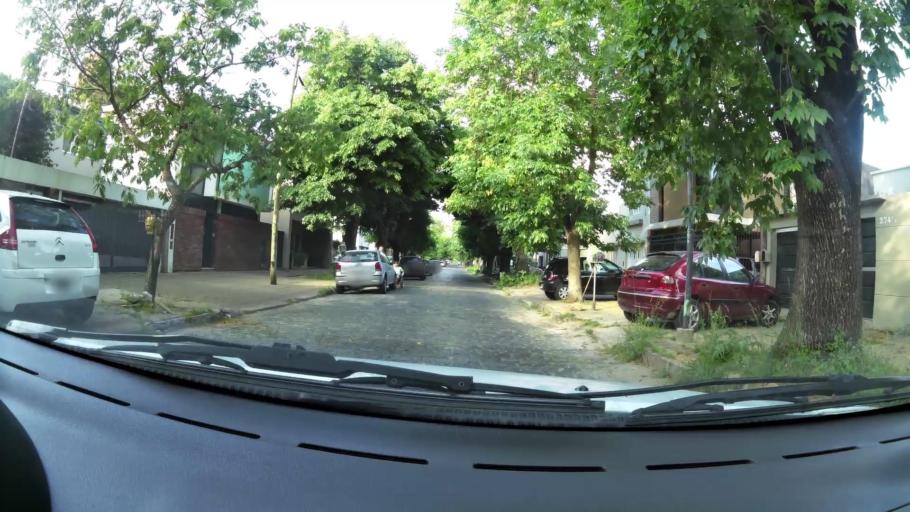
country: AR
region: Buenos Aires
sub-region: Partido de La Plata
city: La Plata
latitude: -34.8963
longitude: -57.9601
